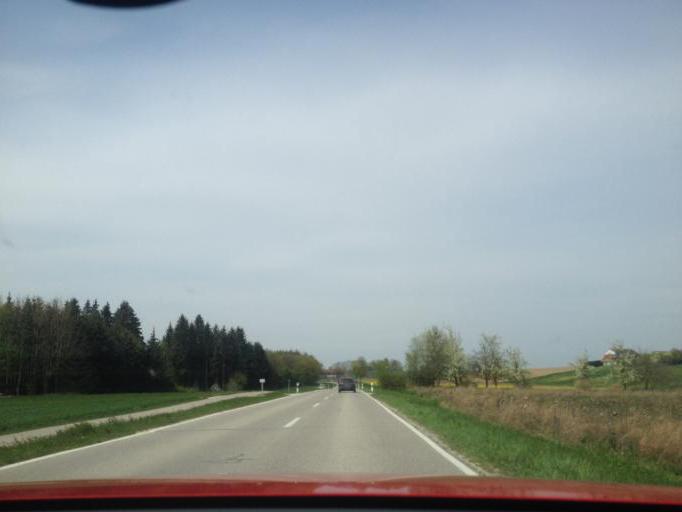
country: DE
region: Bavaria
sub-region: Upper Bavaria
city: Paunzhausen
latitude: 48.4693
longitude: 11.5774
